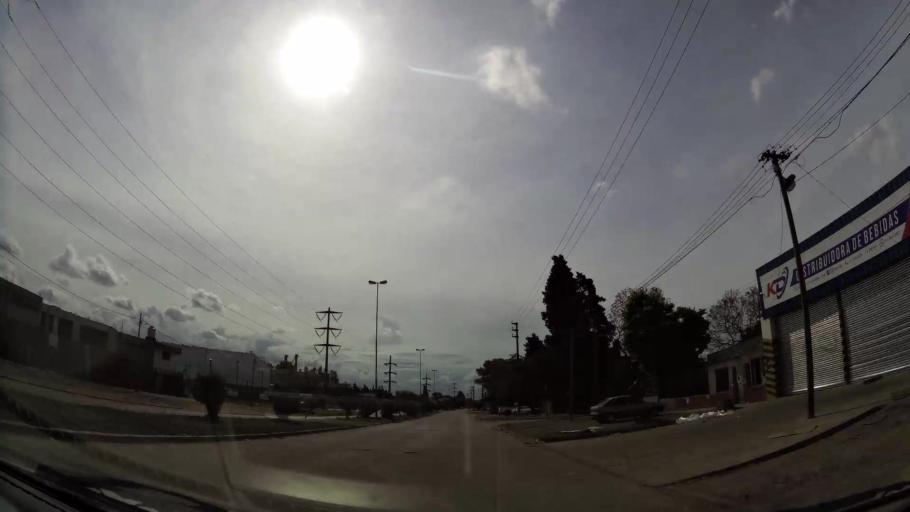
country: AR
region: Buenos Aires
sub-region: Partido de Quilmes
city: Quilmes
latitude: -34.7748
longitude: -58.2392
